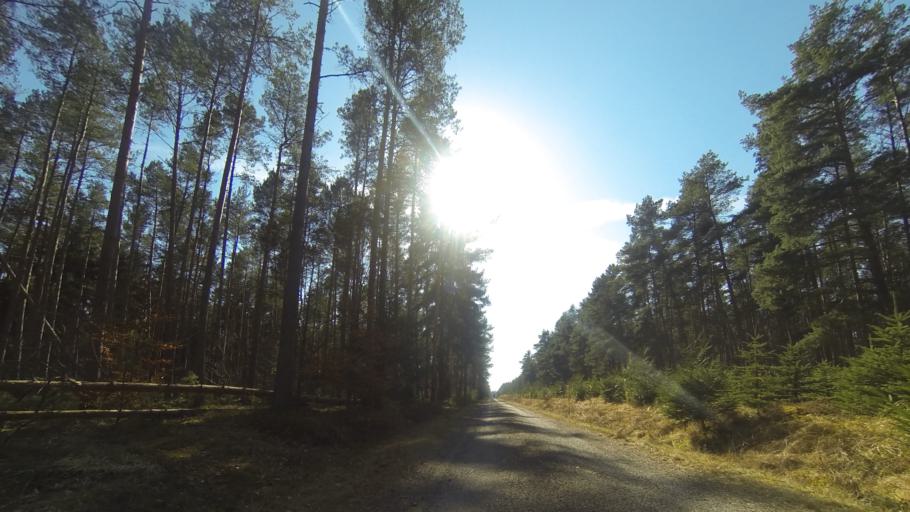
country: DE
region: Saxony
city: Tauscha
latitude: 51.2435
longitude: 13.8233
